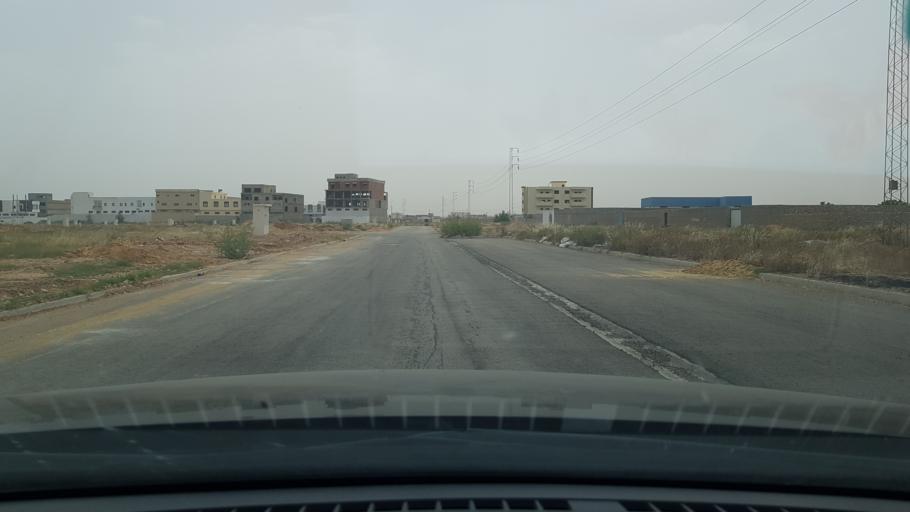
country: TN
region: Safaqis
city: Al Qarmadah
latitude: 34.8298
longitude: 10.7416
